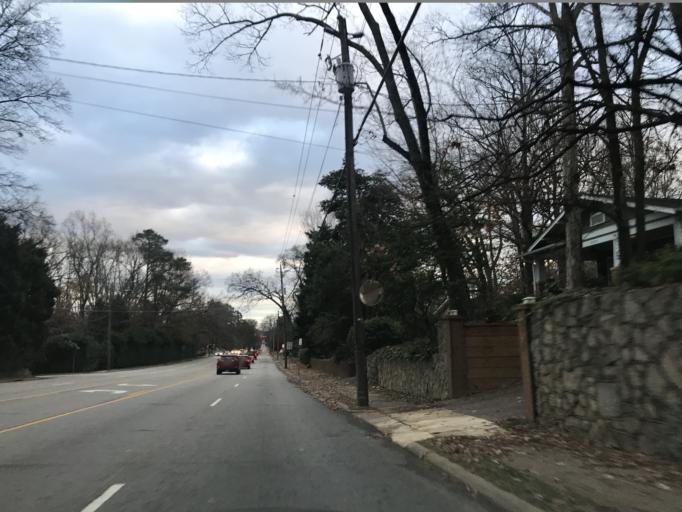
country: US
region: North Carolina
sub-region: Wake County
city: West Raleigh
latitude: 35.8110
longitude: -78.6501
